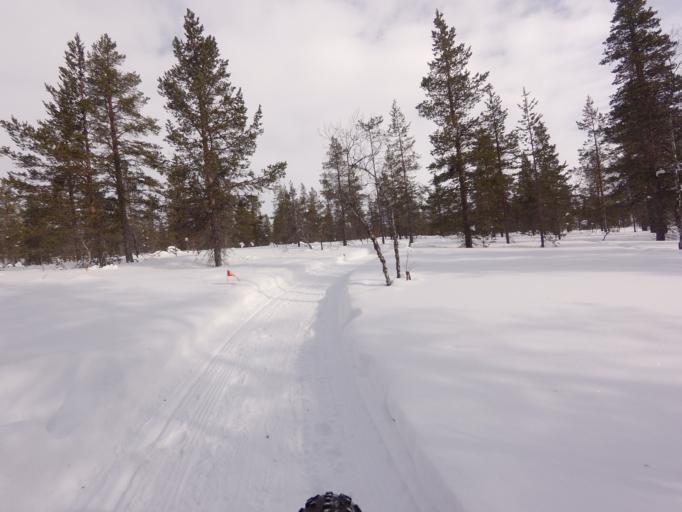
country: FI
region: Lapland
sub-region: Pohjois-Lappi
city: Ivalo
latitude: 68.3463
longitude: 27.4472
